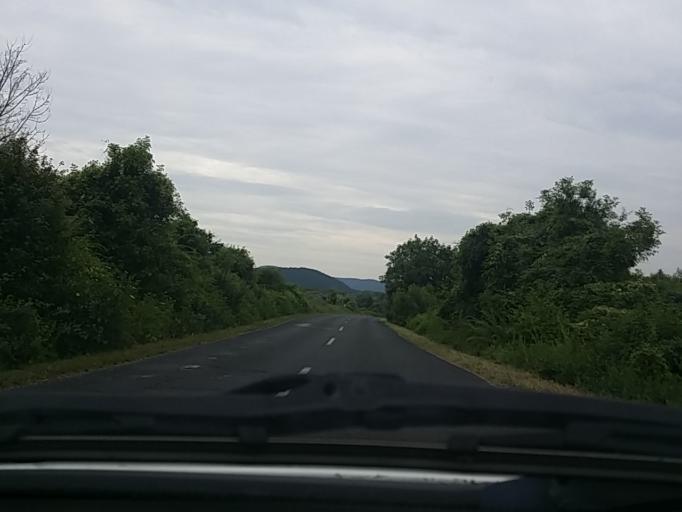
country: HU
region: Pest
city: Csobanka
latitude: 47.6349
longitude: 18.9548
